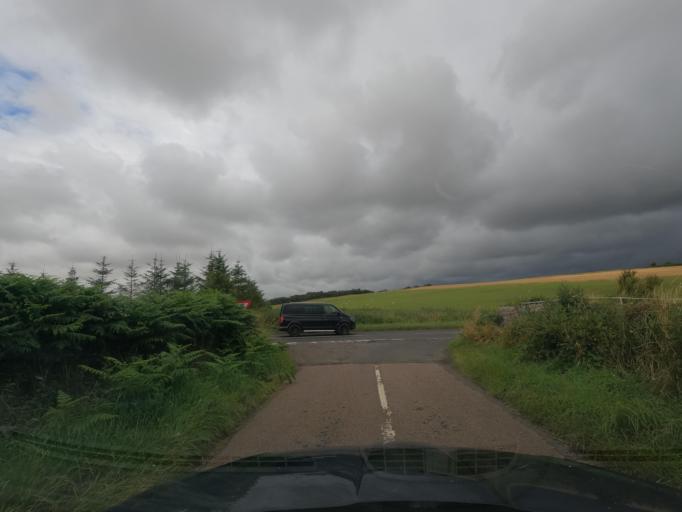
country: GB
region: England
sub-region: Northumberland
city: Ancroft
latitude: 55.7349
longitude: -2.0305
